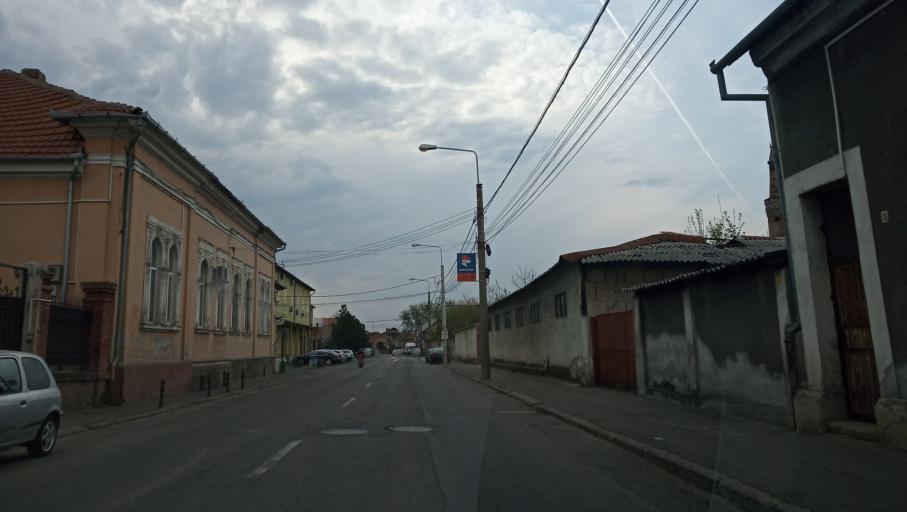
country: RO
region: Bihor
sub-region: Comuna Biharea
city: Oradea
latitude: 47.0496
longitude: 21.9353
